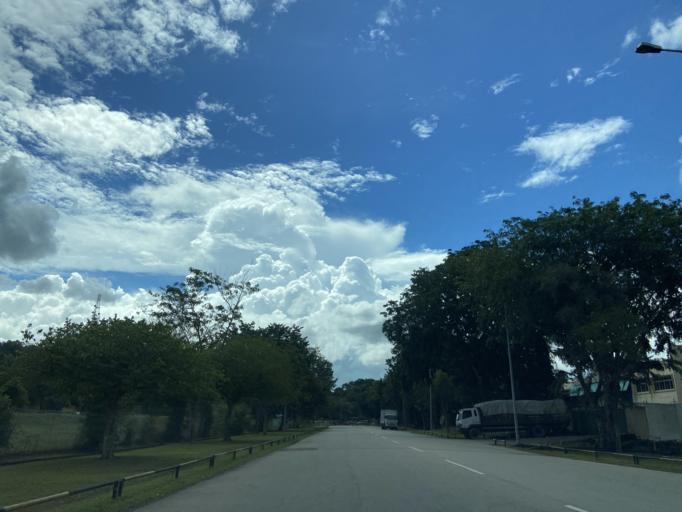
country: SG
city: Singapore
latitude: 1.0614
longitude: 104.0275
